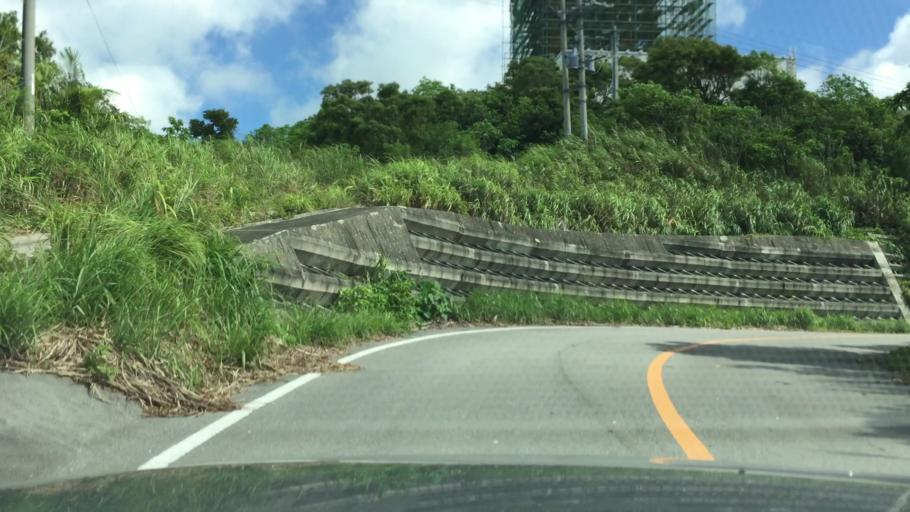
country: JP
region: Okinawa
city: Ishigaki
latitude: 24.3786
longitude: 124.1647
